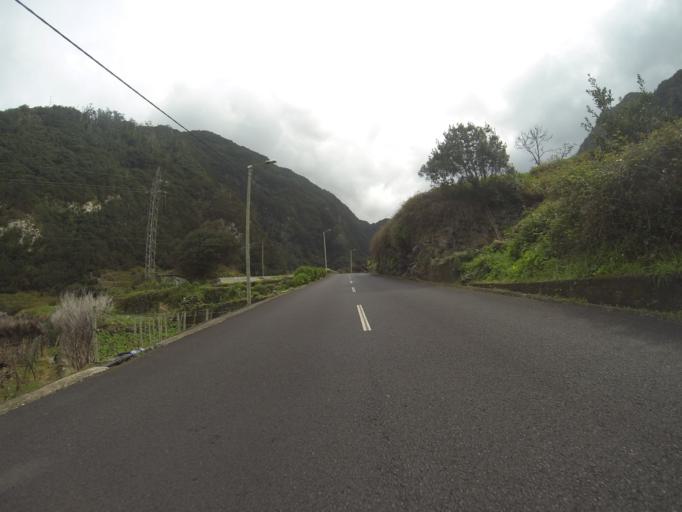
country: PT
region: Madeira
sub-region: Porto Moniz
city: Porto Moniz
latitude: 32.8191
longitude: -17.1095
